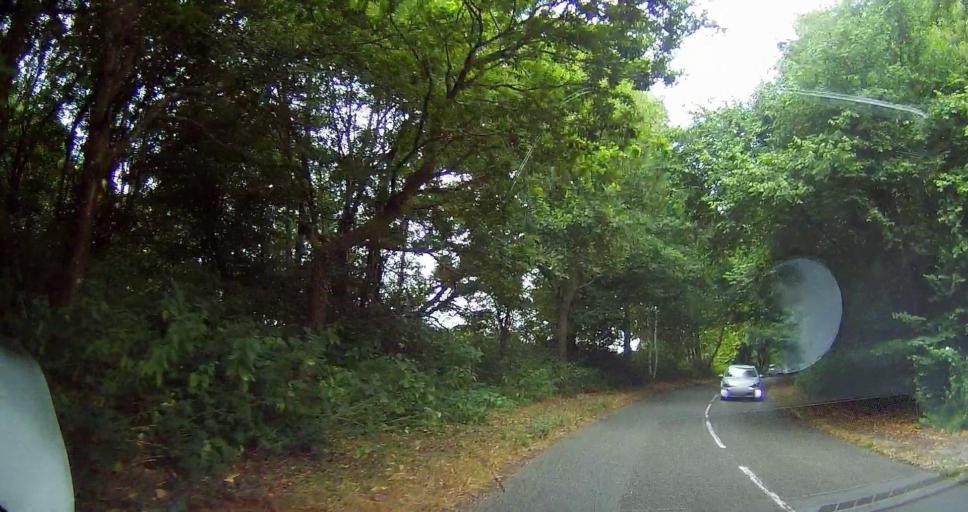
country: GB
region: England
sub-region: East Sussex
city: Wadhurst
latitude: 51.0865
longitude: 0.4017
